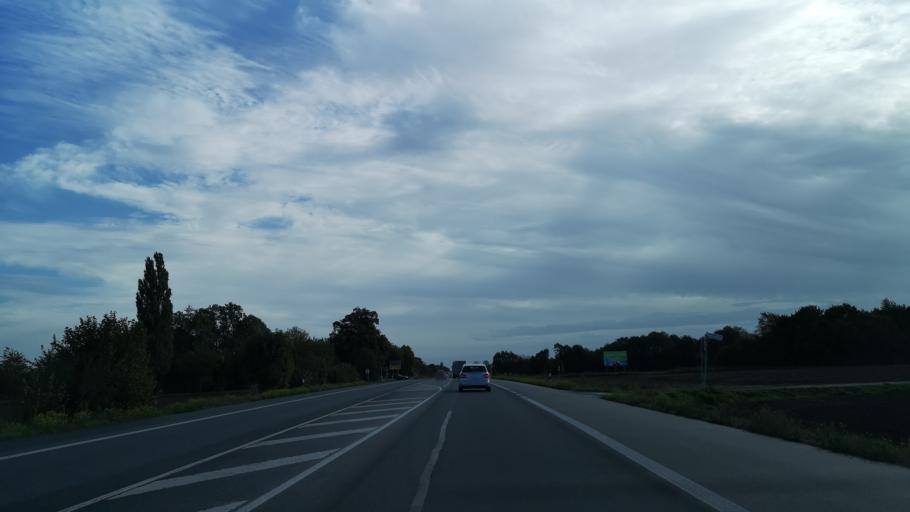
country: DE
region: North Rhine-Westphalia
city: Erwitte
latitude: 51.6181
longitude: 8.3691
